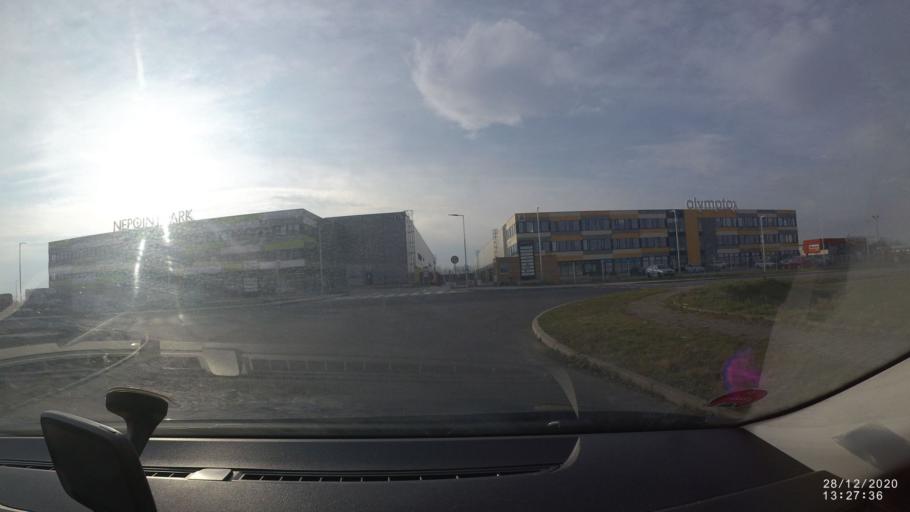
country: CZ
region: Central Bohemia
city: Jirny
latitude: 50.1261
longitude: 14.7131
